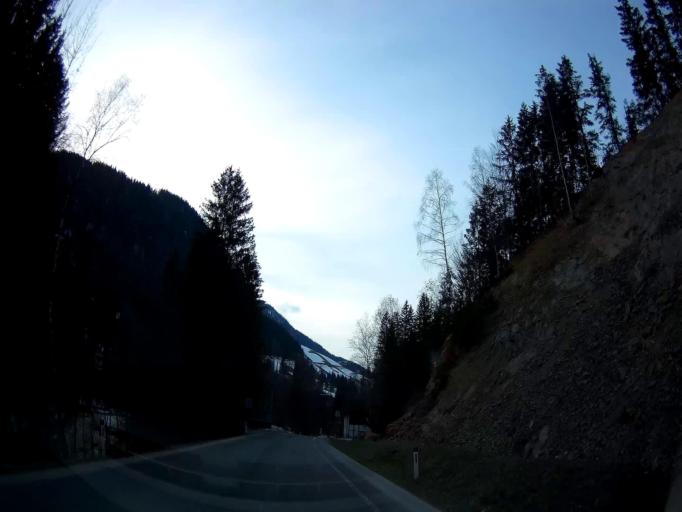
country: AT
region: Salzburg
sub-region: Politischer Bezirk Hallein
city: Abtenau
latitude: 47.5254
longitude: 13.4294
